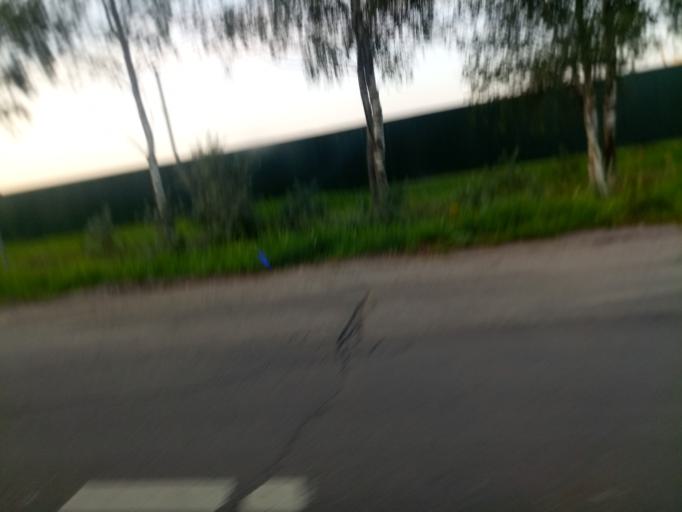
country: RU
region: Moskovskaya
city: Noginsk-9
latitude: 56.0501
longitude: 38.4574
